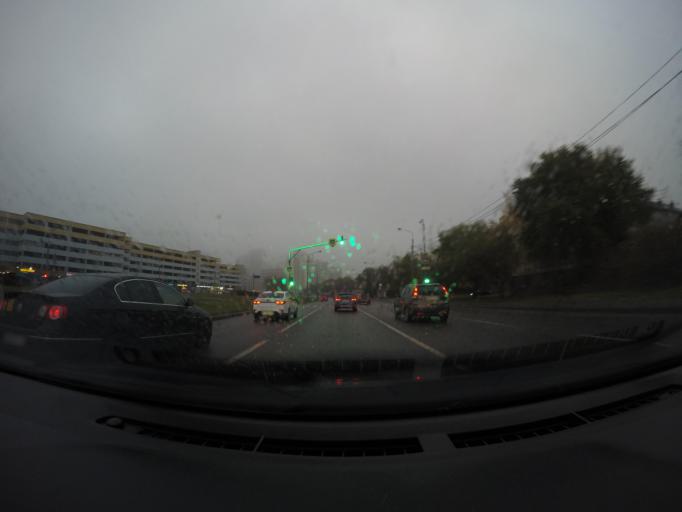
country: RU
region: Moskovskaya
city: Shcherbinka
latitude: 55.5503
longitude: 37.5451
